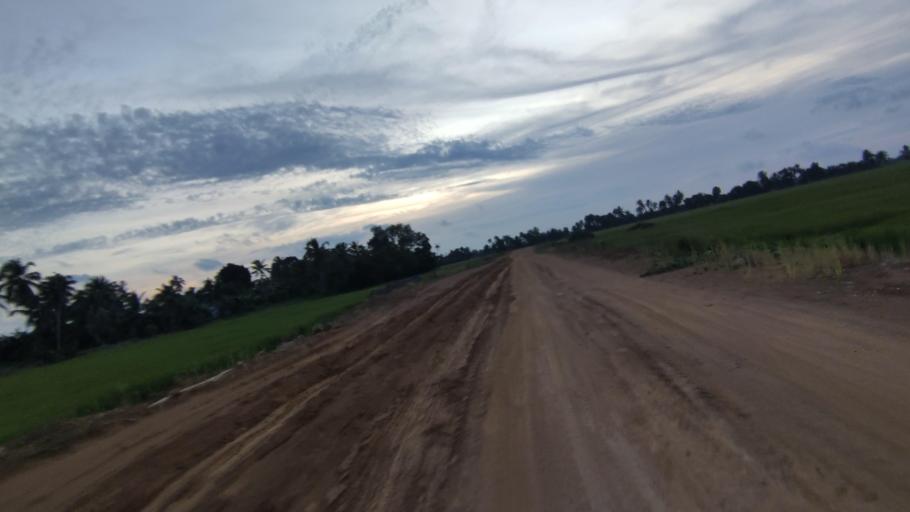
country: IN
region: Kerala
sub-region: Kottayam
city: Kottayam
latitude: 9.6466
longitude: 76.4617
